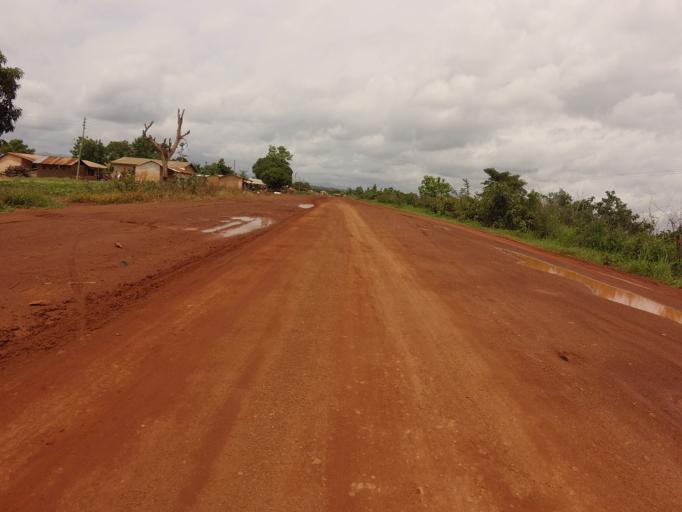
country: GH
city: Kpandae
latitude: 8.4049
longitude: 0.3993
